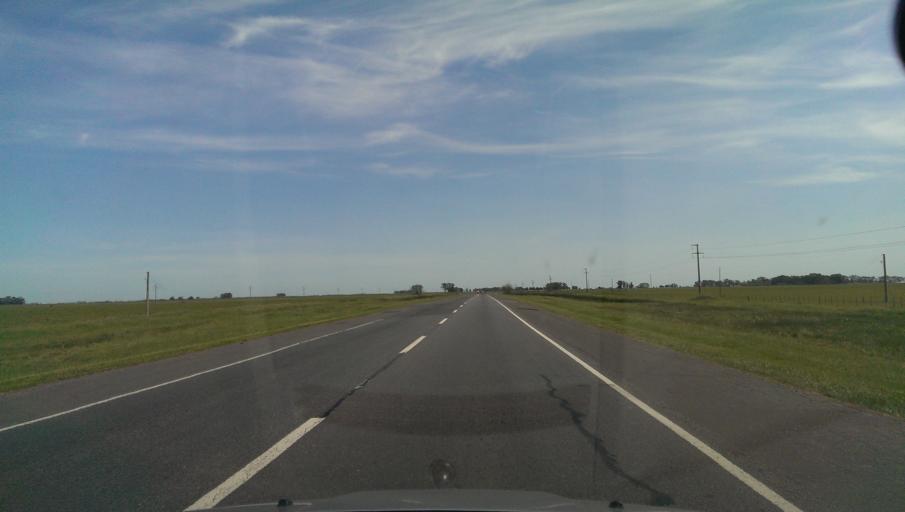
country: AR
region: Buenos Aires
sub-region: Partido de Azul
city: Azul
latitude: -36.4040
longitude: -59.5094
